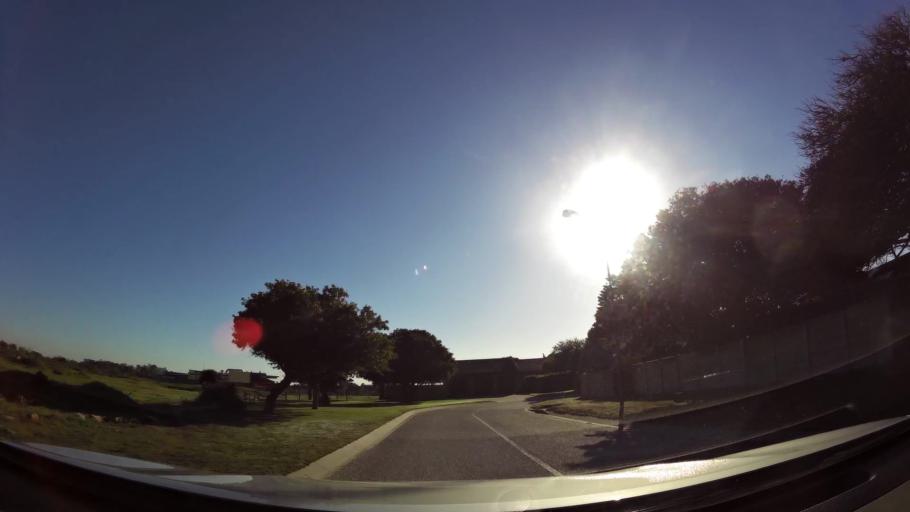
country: ZA
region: Eastern Cape
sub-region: Nelson Mandela Bay Metropolitan Municipality
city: Port Elizabeth
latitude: -33.9927
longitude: 25.6473
